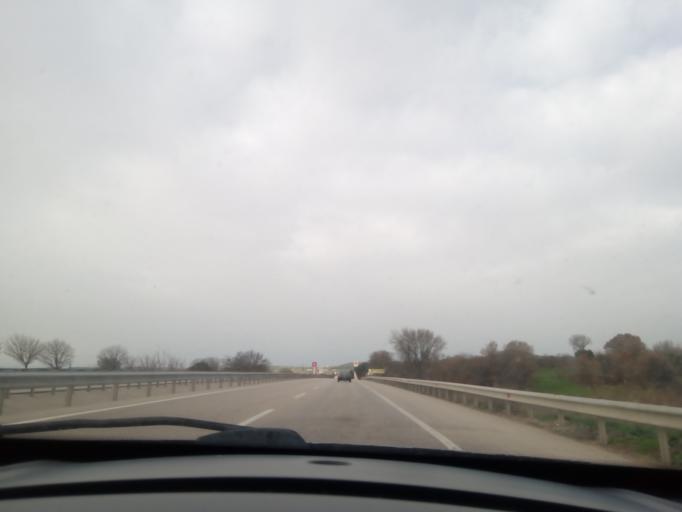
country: TR
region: Bursa
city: Gorukle
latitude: 40.2145
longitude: 28.7373
